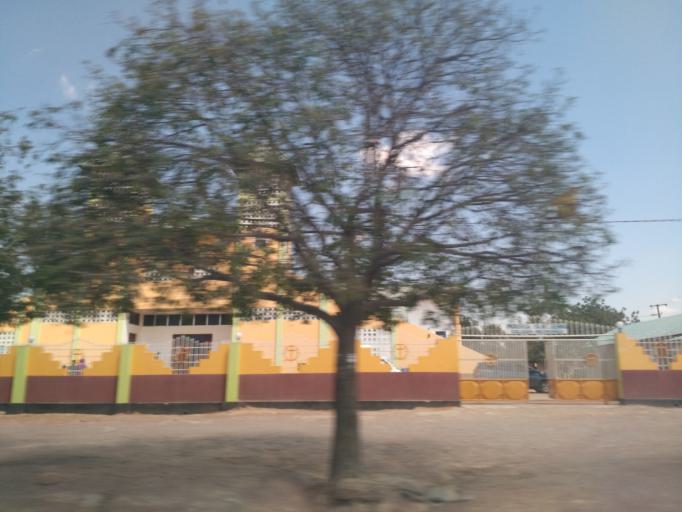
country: TZ
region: Dodoma
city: Dodoma
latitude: -6.1528
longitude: 35.7250
